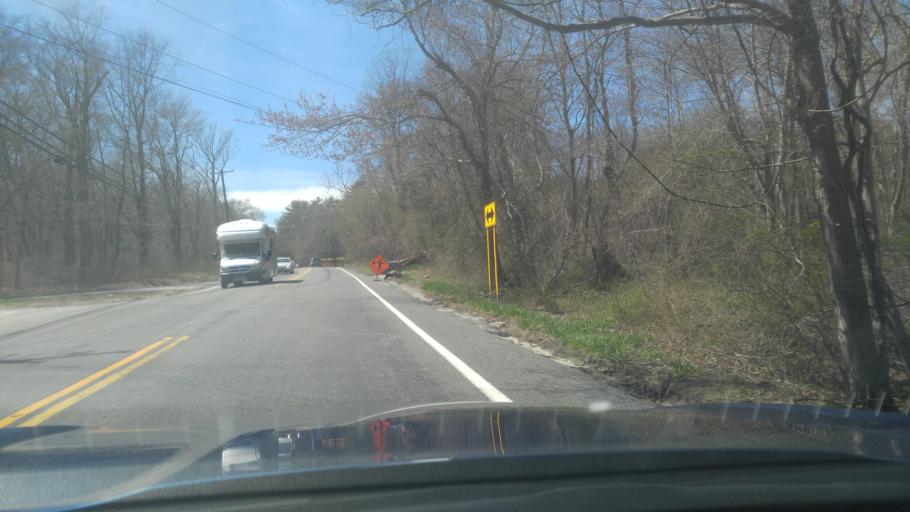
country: US
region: Rhode Island
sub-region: Washington County
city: Exeter
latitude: 41.5793
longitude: -71.6018
